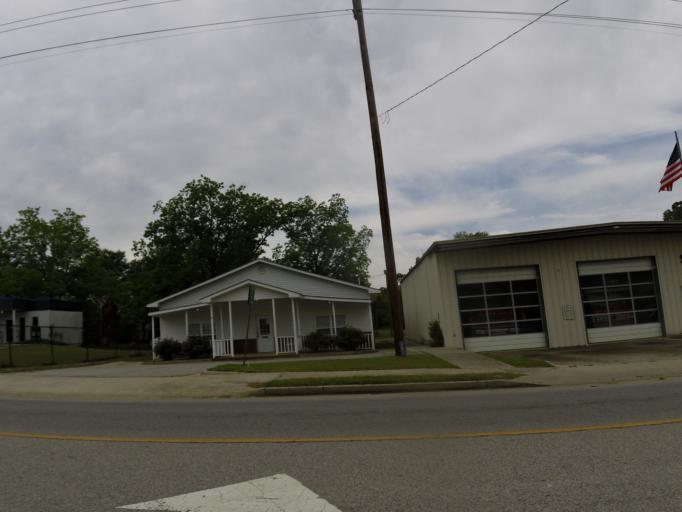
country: US
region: Georgia
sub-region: Emanuel County
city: Twin City
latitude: 32.4415
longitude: -82.2154
